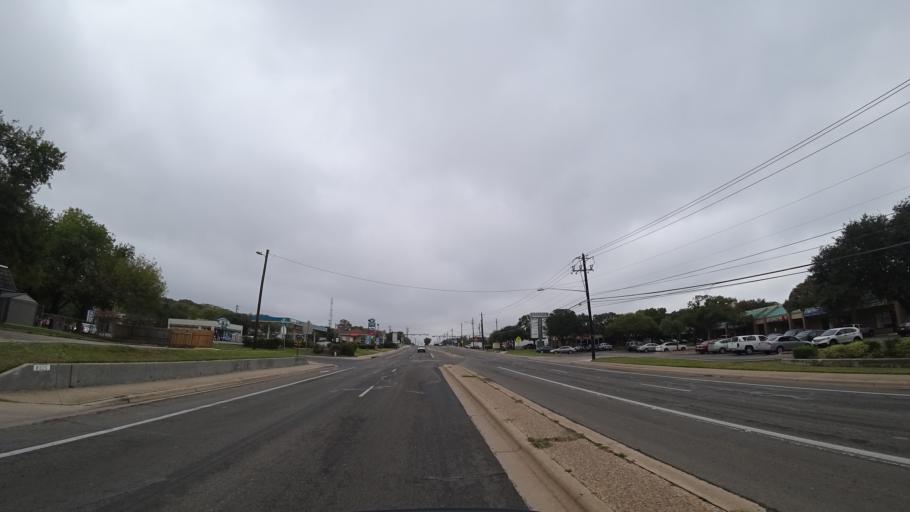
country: US
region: Texas
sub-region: Travis County
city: Shady Hollow
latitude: 30.2023
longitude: -97.8378
